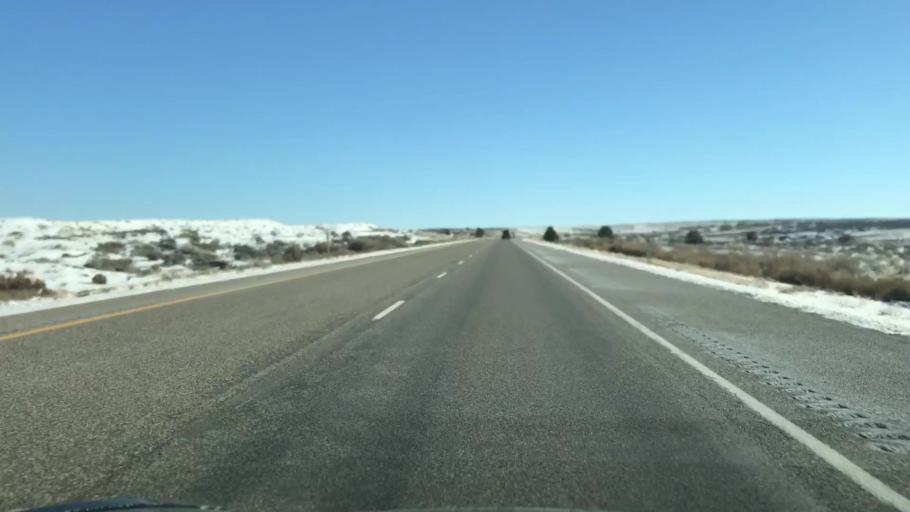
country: US
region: Colorado
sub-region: Mesa County
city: Loma
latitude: 39.1933
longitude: -109.0678
